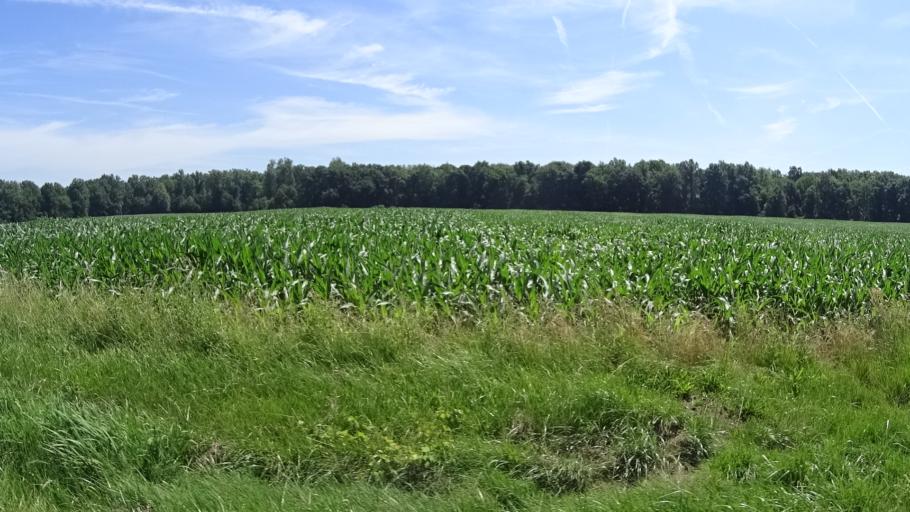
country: US
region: Ohio
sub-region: Lorain County
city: Vermilion
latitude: 41.3605
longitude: -82.4360
